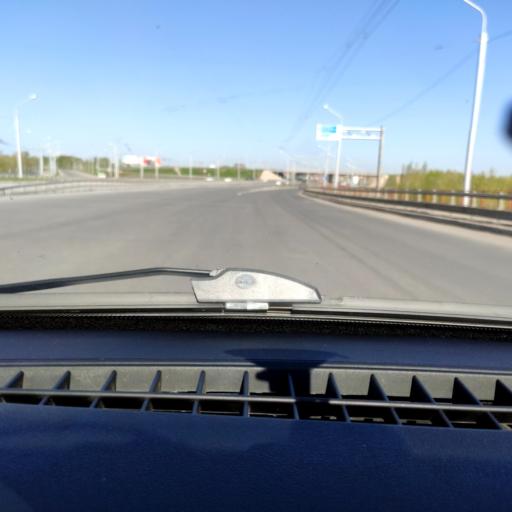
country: RU
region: Bashkortostan
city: Ufa
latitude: 54.7615
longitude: 55.9607
